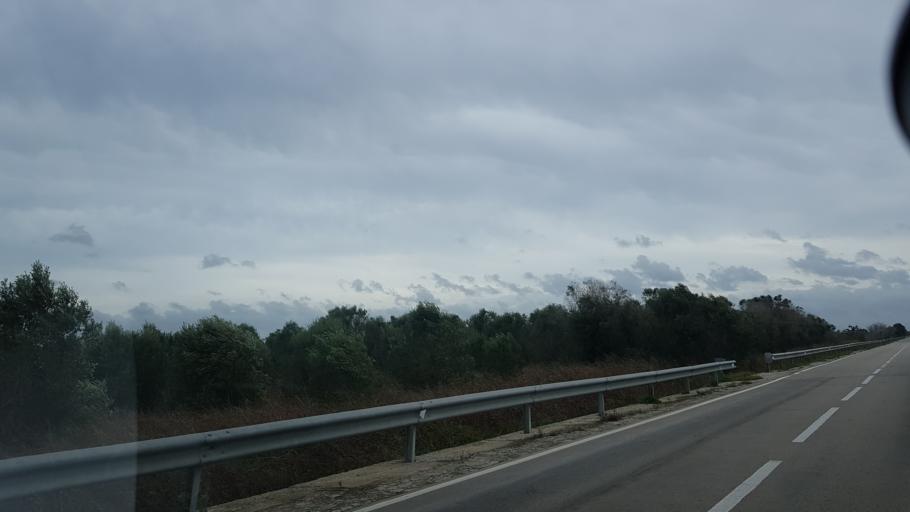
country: IT
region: Apulia
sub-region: Provincia di Brindisi
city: San Donaci
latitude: 40.4043
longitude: 17.8979
